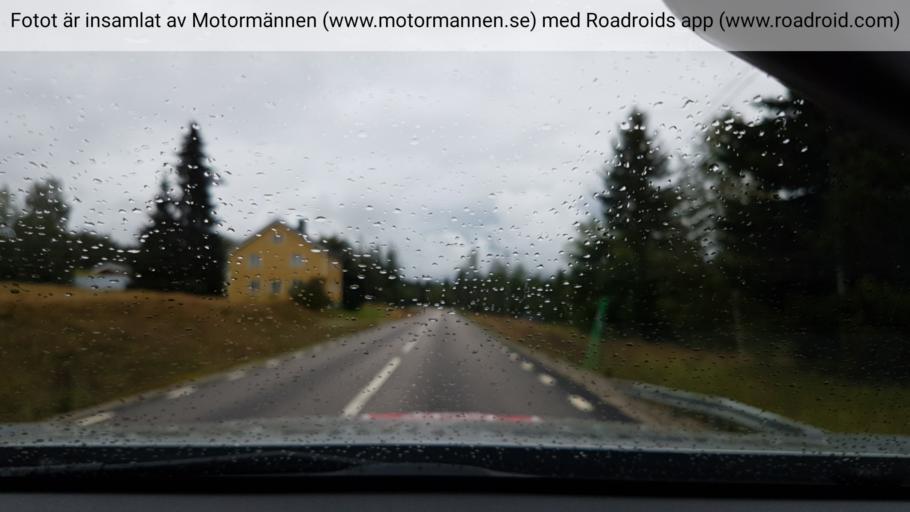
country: SE
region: Vaesterbotten
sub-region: Asele Kommun
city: Insjon
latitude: 64.7154
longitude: 17.6821
